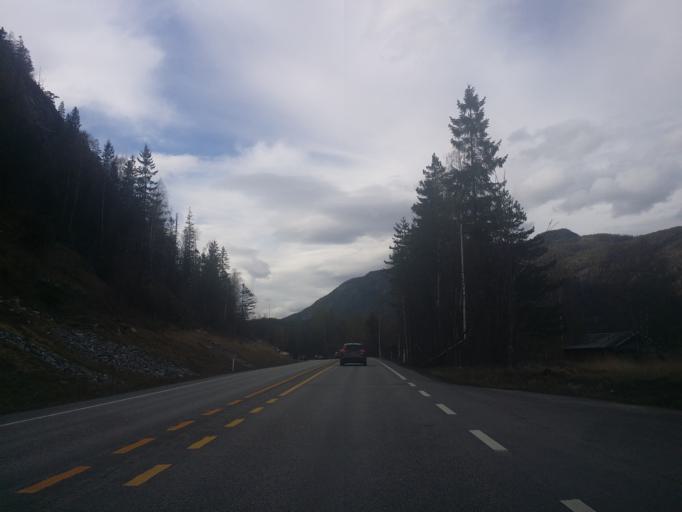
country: NO
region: Buskerud
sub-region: Nes
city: Nesbyen
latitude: 60.4627
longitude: 9.2533
